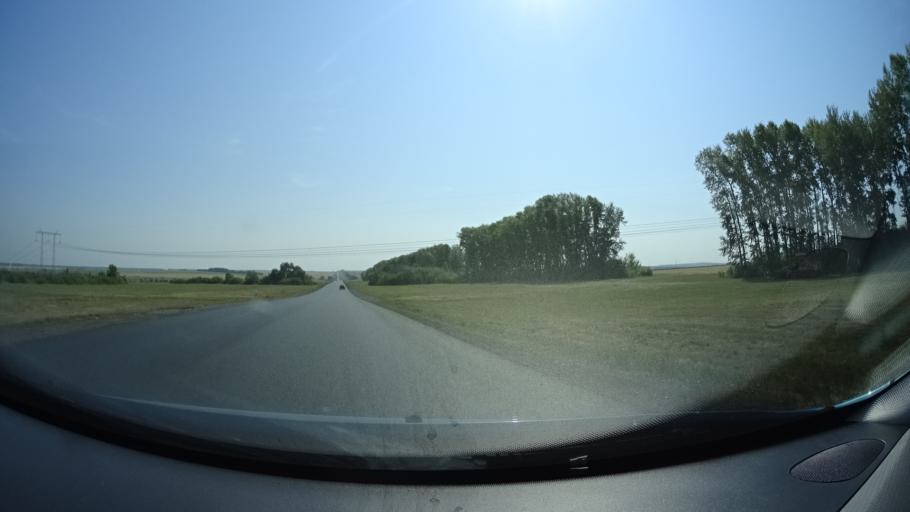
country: RU
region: Bashkortostan
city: Kabakovo
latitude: 54.4443
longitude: 55.9893
